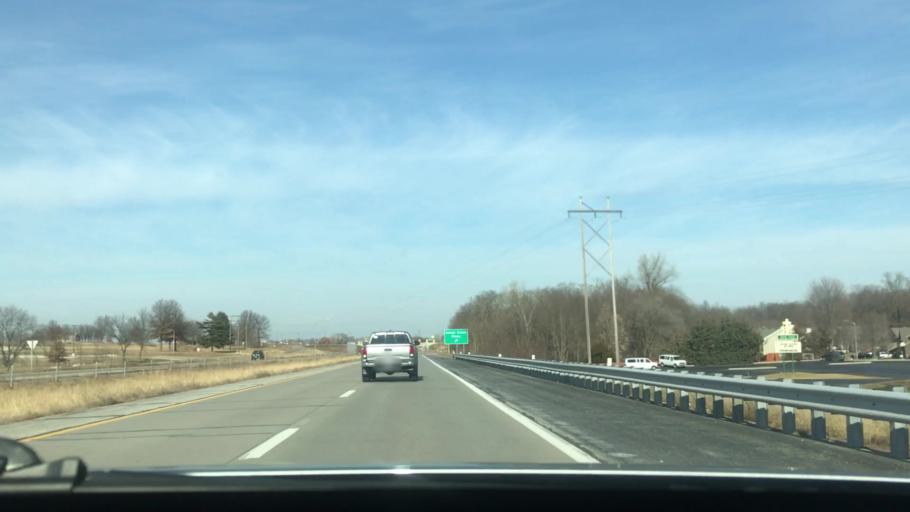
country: US
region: Missouri
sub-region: Clay County
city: Gladstone
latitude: 39.2825
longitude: -94.5849
